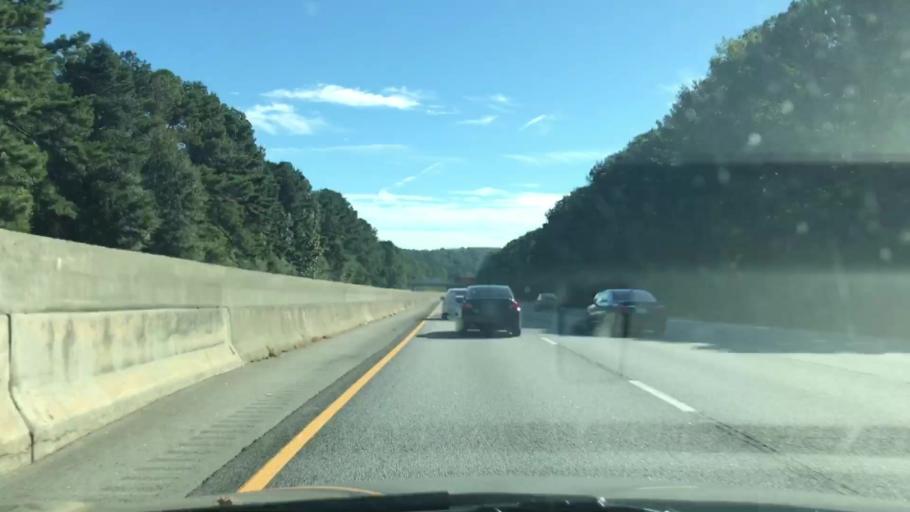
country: US
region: Georgia
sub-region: DeKalb County
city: Stone Mountain
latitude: 33.8209
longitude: -84.1647
